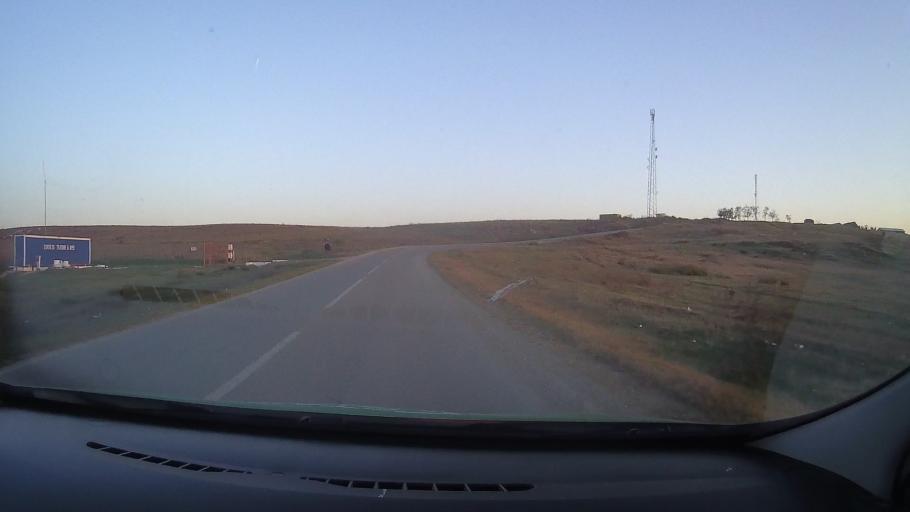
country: RO
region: Timis
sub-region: Comuna Manastiur
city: Manastiur
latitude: 45.8262
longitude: 22.0712
